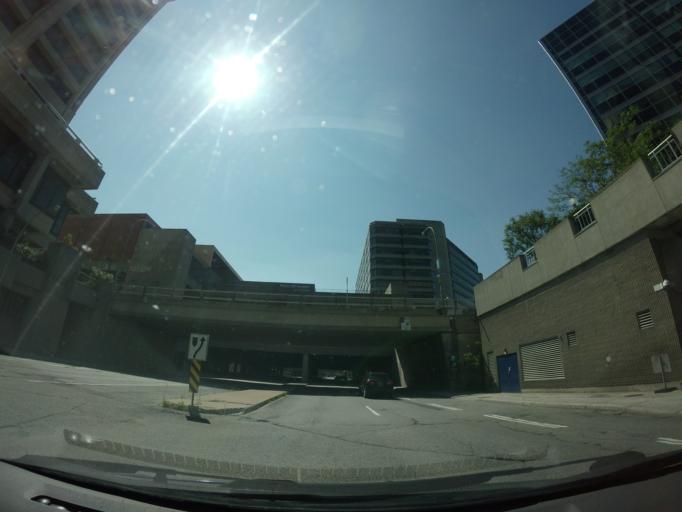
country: CA
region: Ontario
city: Ottawa
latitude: 45.4278
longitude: -75.7141
